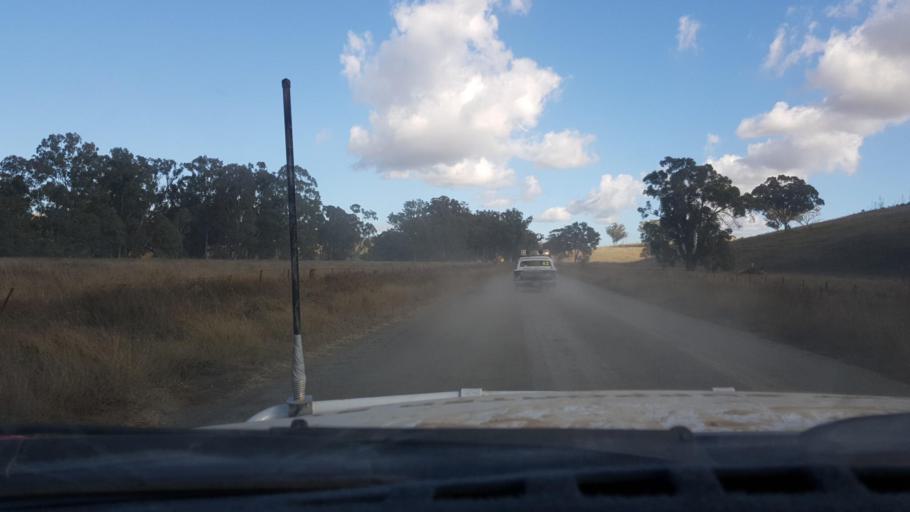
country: AU
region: New South Wales
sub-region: Tamworth Municipality
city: Manilla
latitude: -30.6130
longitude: 150.5131
